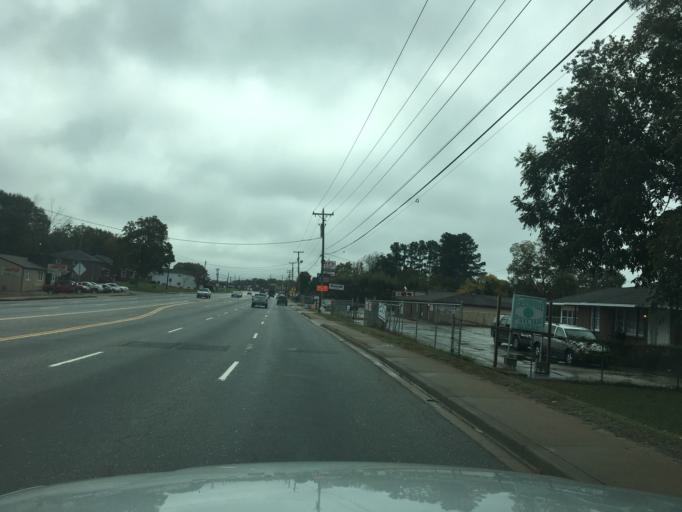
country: US
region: South Carolina
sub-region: Greenville County
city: Welcome
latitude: 34.8240
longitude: -82.4472
